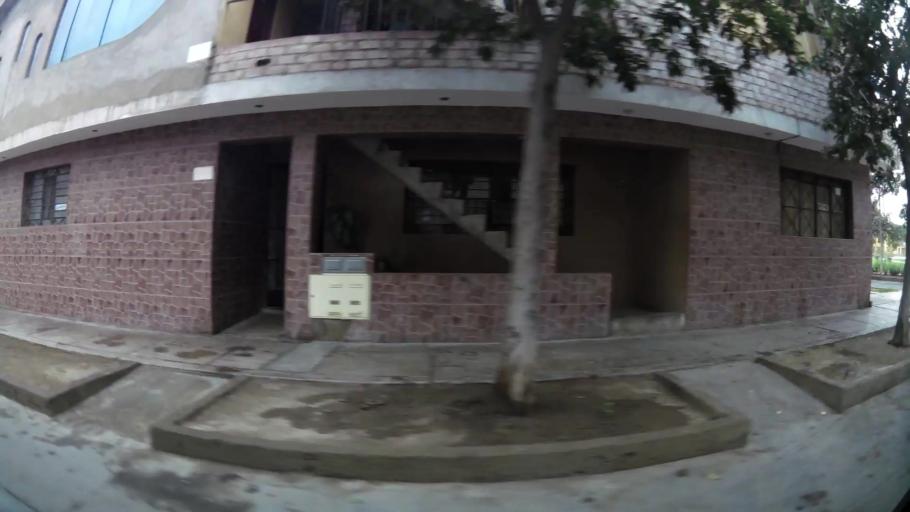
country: PE
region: Lima
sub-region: Lima
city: Independencia
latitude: -11.9756
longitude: -77.0705
